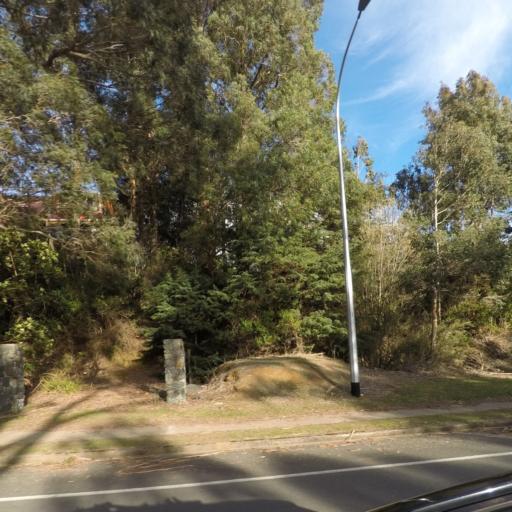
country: NZ
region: Manawatu-Wanganui
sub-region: Ruapehu District
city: Waiouru
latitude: -39.4063
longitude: 175.4094
